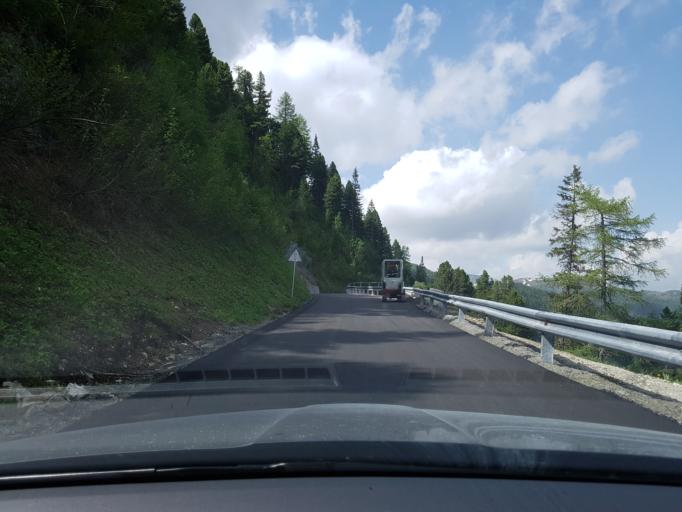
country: AT
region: Salzburg
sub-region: Politischer Bezirk Tamsweg
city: Thomatal
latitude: 46.9747
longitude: 13.7696
